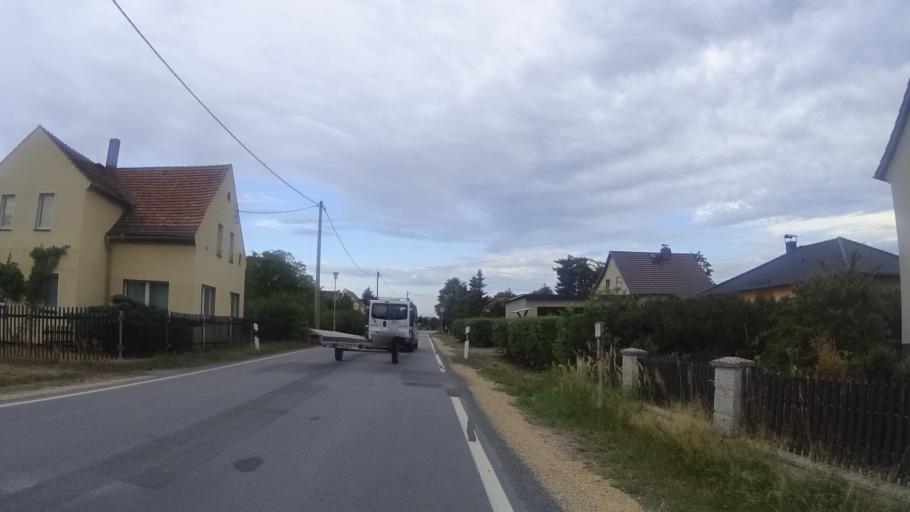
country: DE
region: Saxony
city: Rothenburg
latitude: 51.3135
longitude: 14.9941
